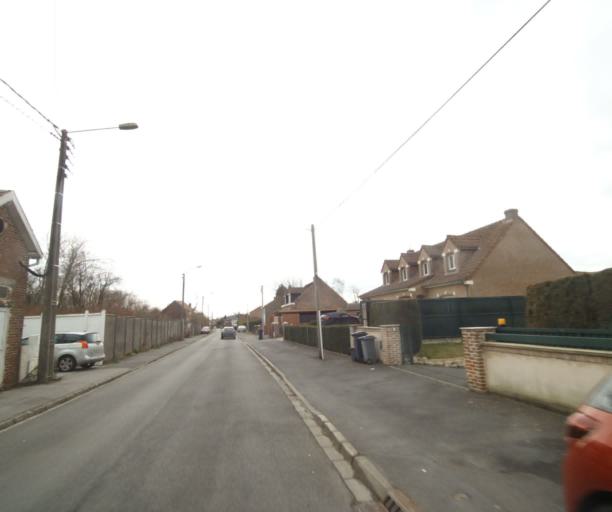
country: FR
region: Nord-Pas-de-Calais
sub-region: Departement du Nord
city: Saint-Saulve
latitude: 50.3618
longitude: 3.5557
